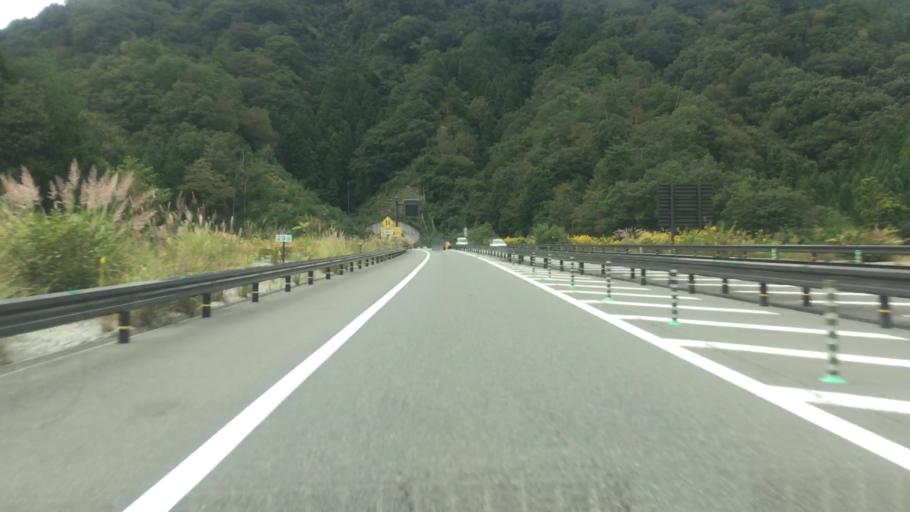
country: JP
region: Hyogo
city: Toyooka
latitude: 35.3443
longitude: 134.8043
